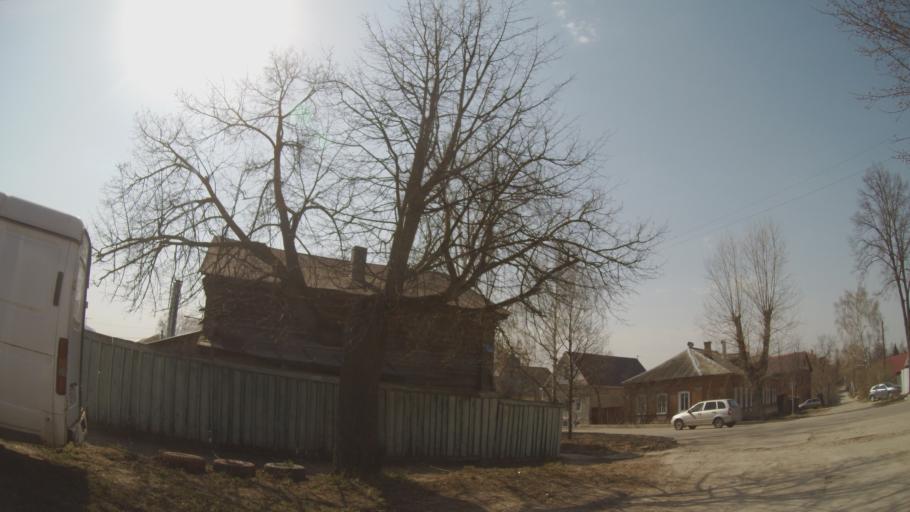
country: RU
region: Nizjnij Novgorod
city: Arzamas
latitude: 55.3907
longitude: 43.8235
